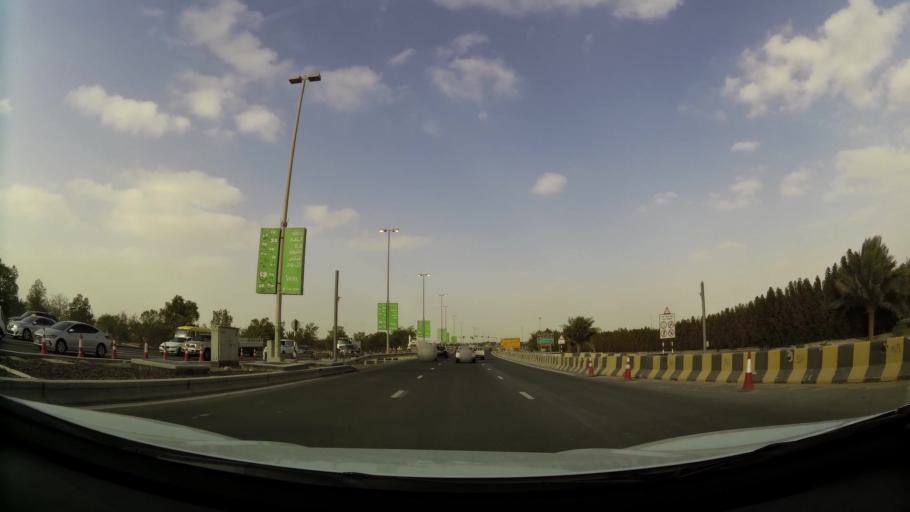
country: AE
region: Abu Dhabi
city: Abu Dhabi
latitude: 24.4561
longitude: 54.6188
